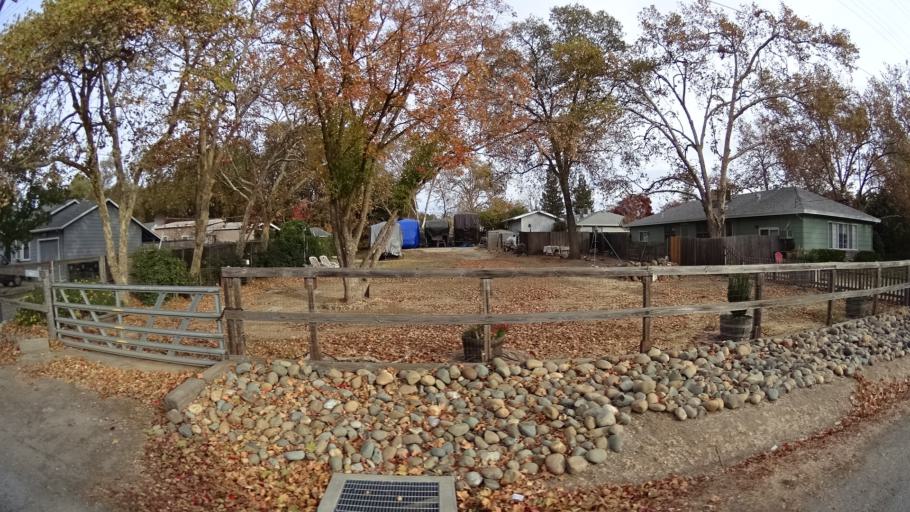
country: US
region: California
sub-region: Sacramento County
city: Citrus Heights
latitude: 38.7076
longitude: -121.2785
